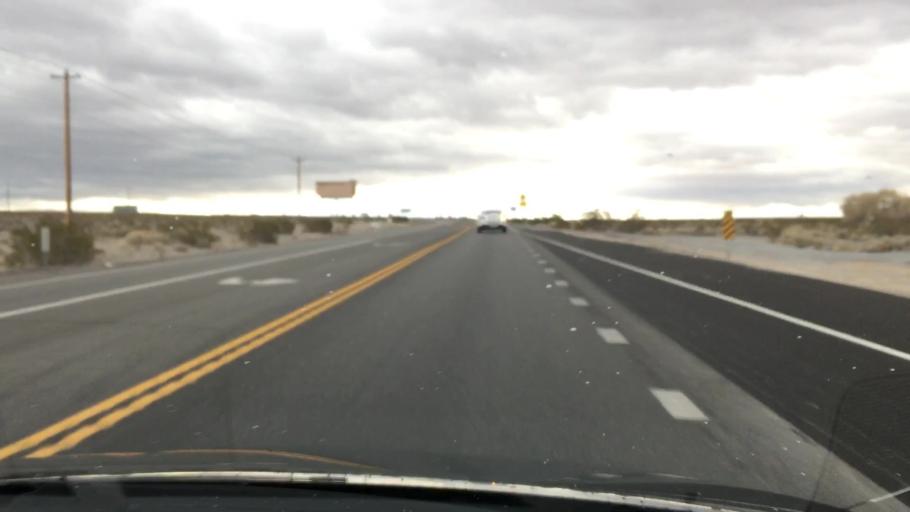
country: US
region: Nevada
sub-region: Nye County
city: Pahrump
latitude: 36.1522
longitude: -115.8961
